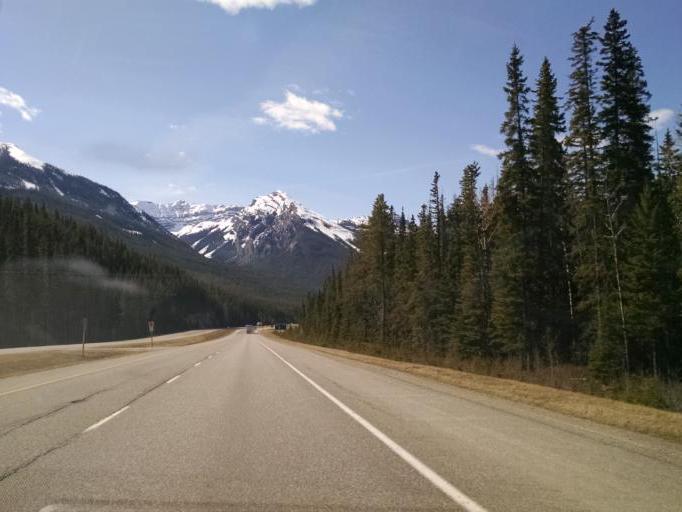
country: CA
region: Alberta
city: Banff
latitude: 51.1579
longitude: -115.6948
